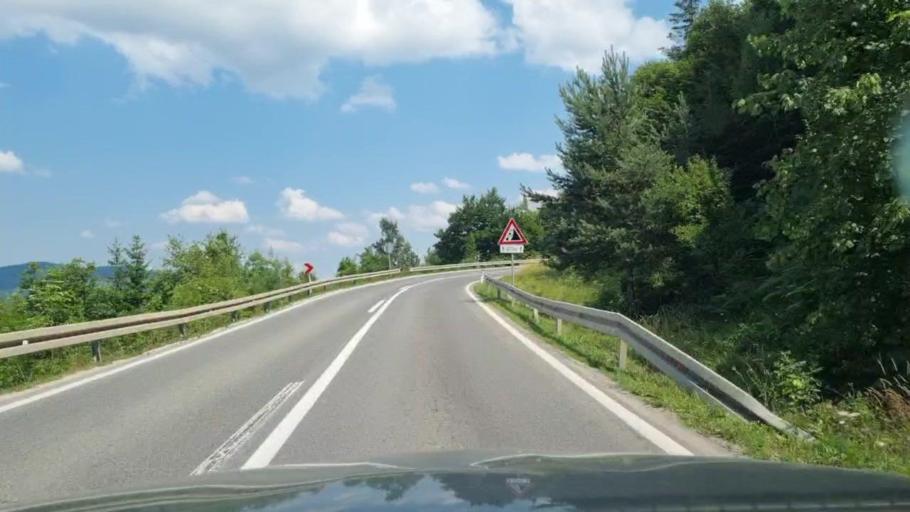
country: BA
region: Federation of Bosnia and Herzegovina
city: Kladanj
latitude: 44.2587
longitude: 18.7264
